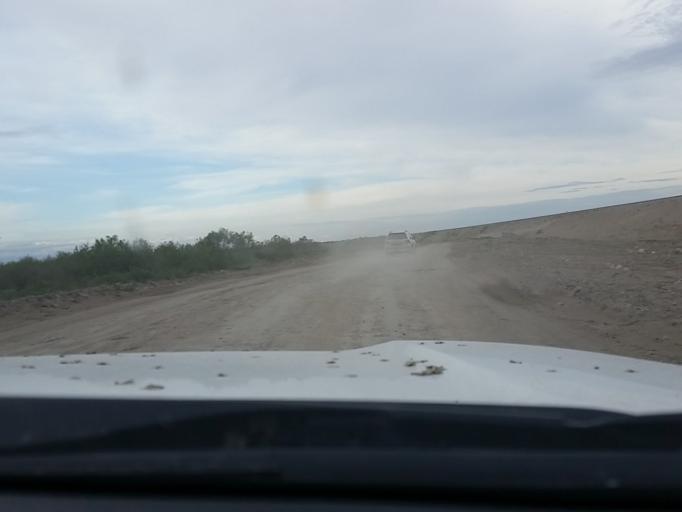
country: KZ
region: Almaty Oblysy
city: Zharkent
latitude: 44.1035
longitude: 80.0844
